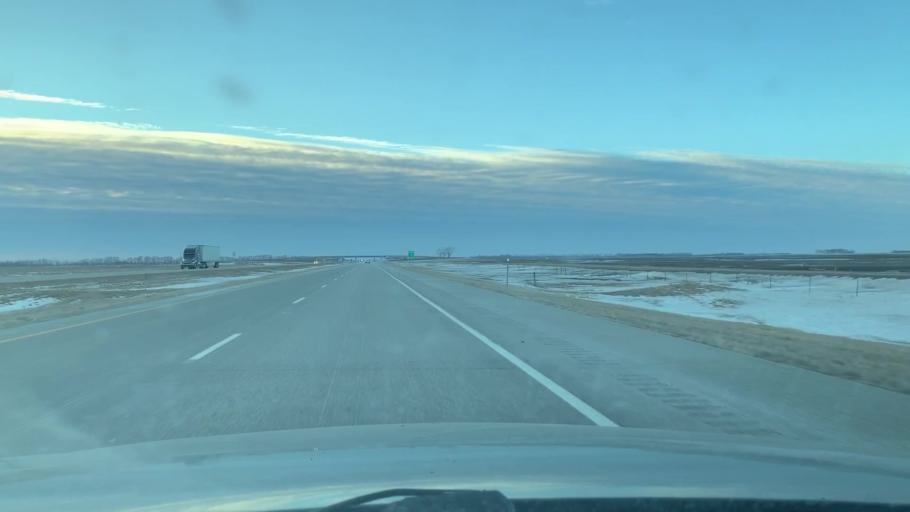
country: US
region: North Dakota
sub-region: Cass County
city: Casselton
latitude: 46.8758
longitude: -97.4815
